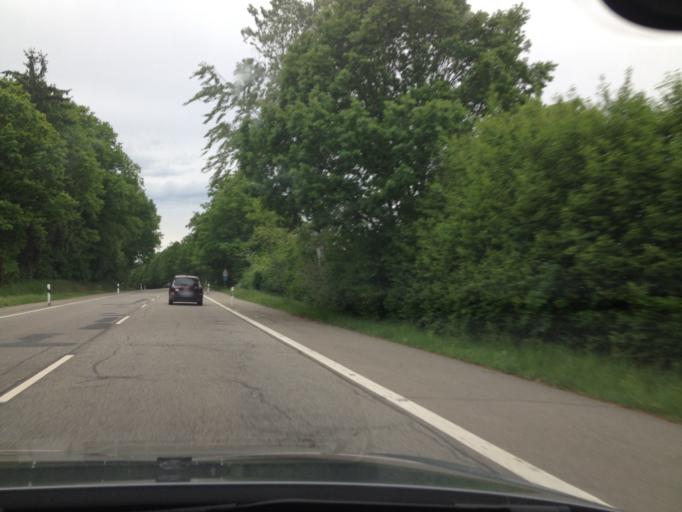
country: DE
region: Saarland
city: Kirkel
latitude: 49.3024
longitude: 7.2608
